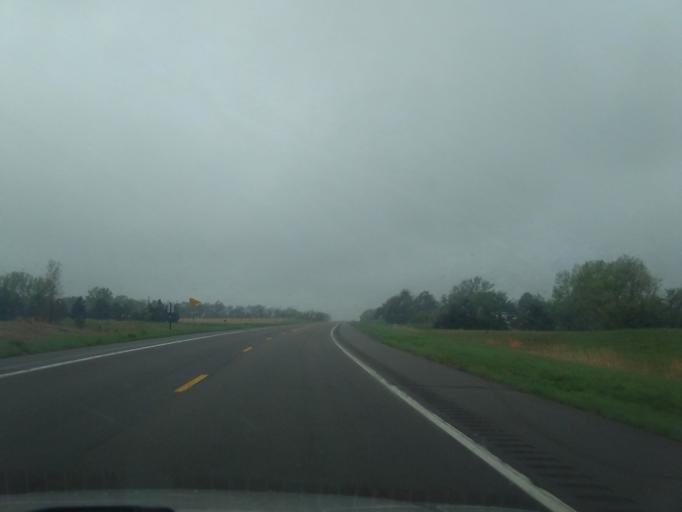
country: US
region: Nebraska
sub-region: Madison County
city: Norfolk
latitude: 42.0775
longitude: -97.3282
